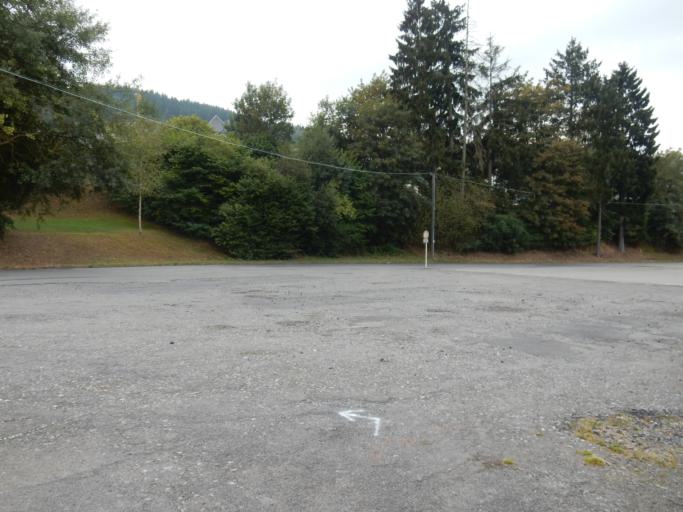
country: LU
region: Diekirch
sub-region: Canton de Wiltz
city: Wiltz
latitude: 49.9672
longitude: 5.9286
